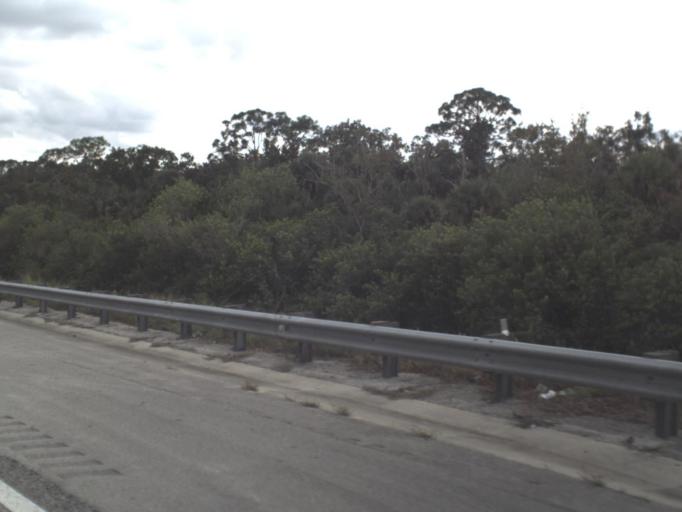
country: US
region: Florida
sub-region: Martin County
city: Palm City
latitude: 27.1142
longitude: -80.2727
